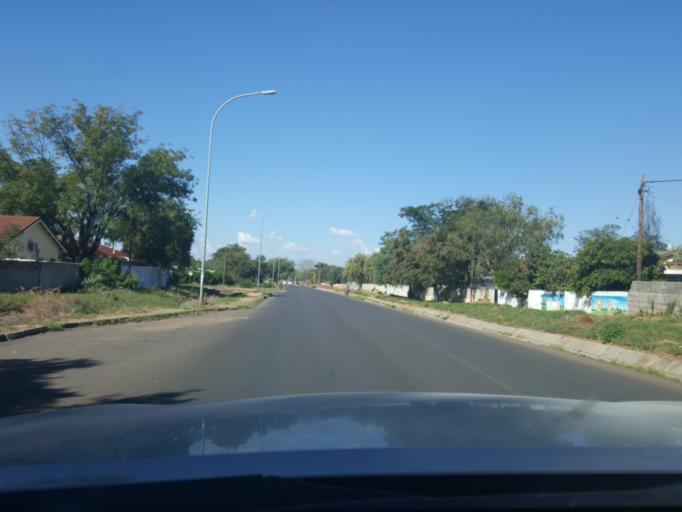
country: BW
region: South East
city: Gaborone
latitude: -24.6263
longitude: 25.9399
